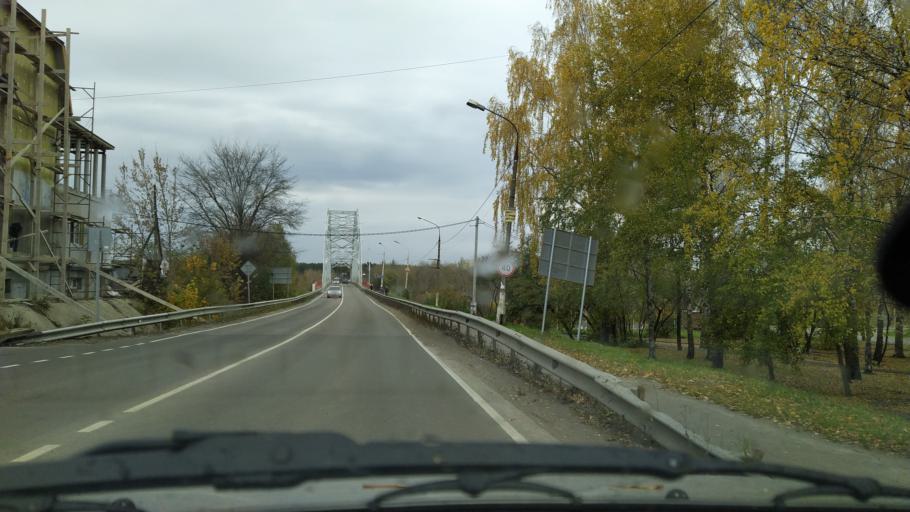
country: RU
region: Moskovskaya
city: Voskresensk
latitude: 55.3194
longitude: 38.6507
